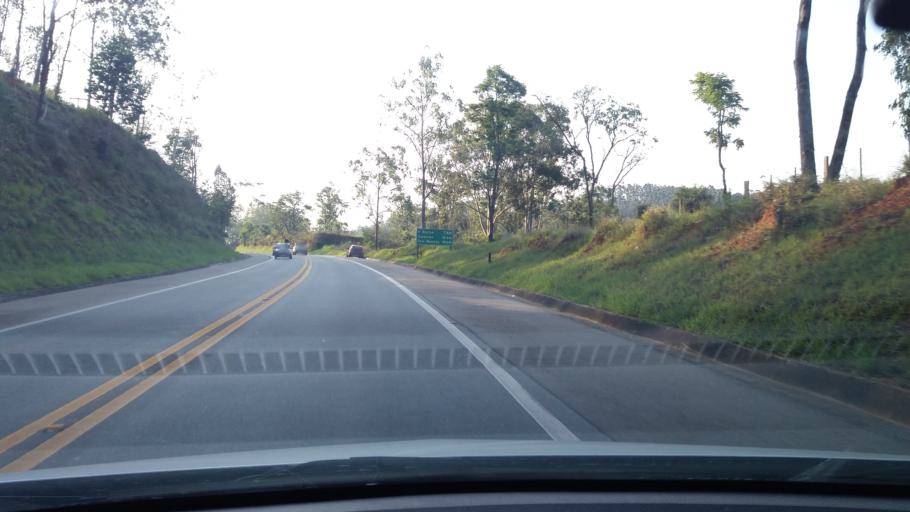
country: BR
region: Sao Paulo
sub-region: Franco Da Rocha
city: Franco da Rocha
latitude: -23.3347
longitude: -46.6655
